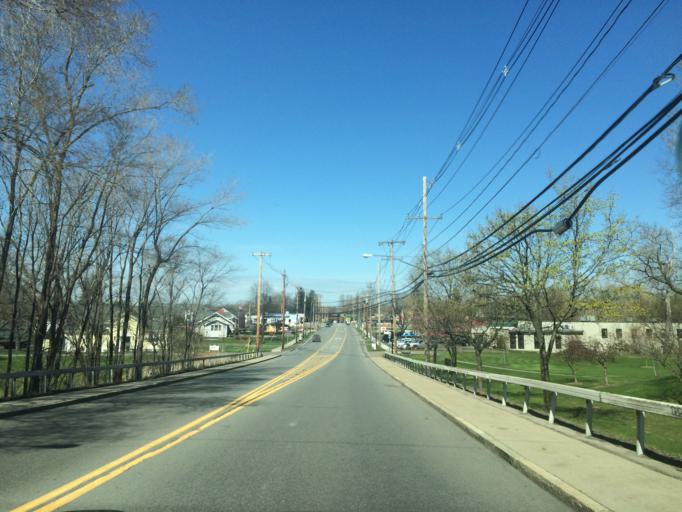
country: US
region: New York
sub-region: Monroe County
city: Fairport
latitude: 43.1005
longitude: -77.4582
